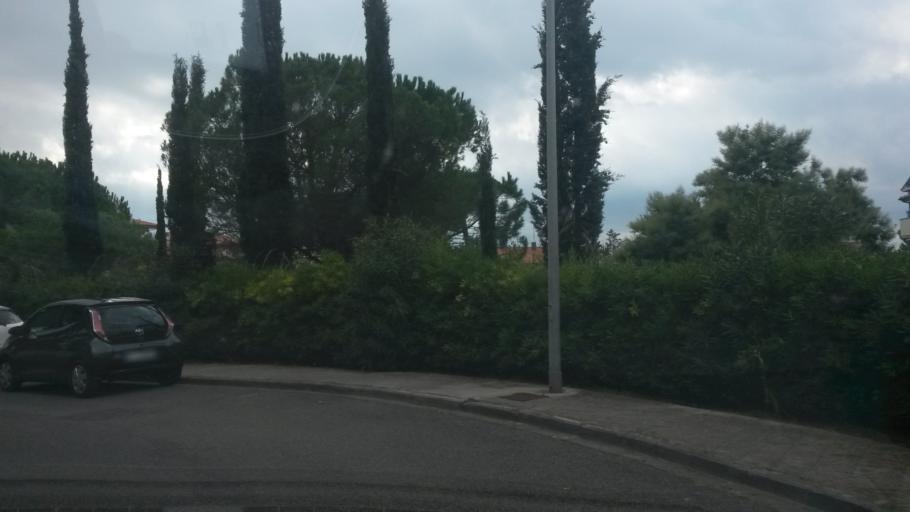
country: IT
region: Tuscany
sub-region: Provincia di Livorno
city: Rosignano Solvay-Castiglioncello
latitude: 43.4031
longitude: 10.4389
